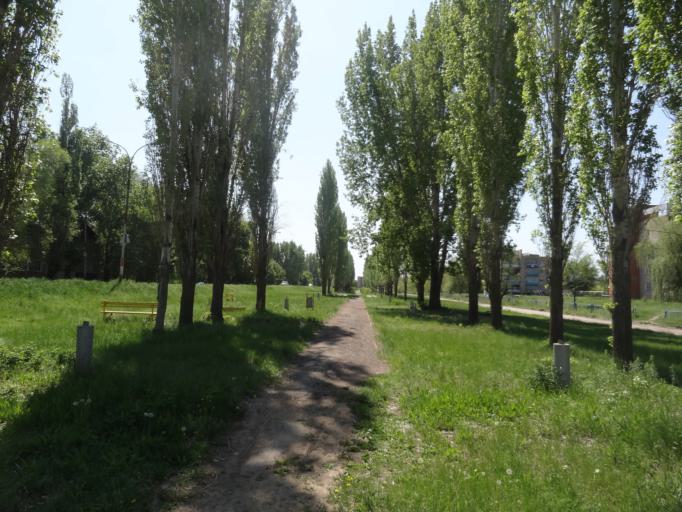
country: RU
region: Saratov
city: Privolzhskiy
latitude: 51.3950
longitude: 46.1295
